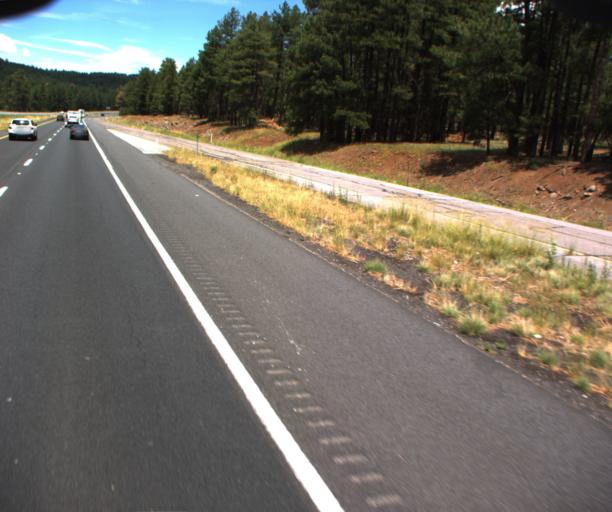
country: US
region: Arizona
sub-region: Coconino County
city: Sedona
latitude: 34.9543
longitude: -111.6729
